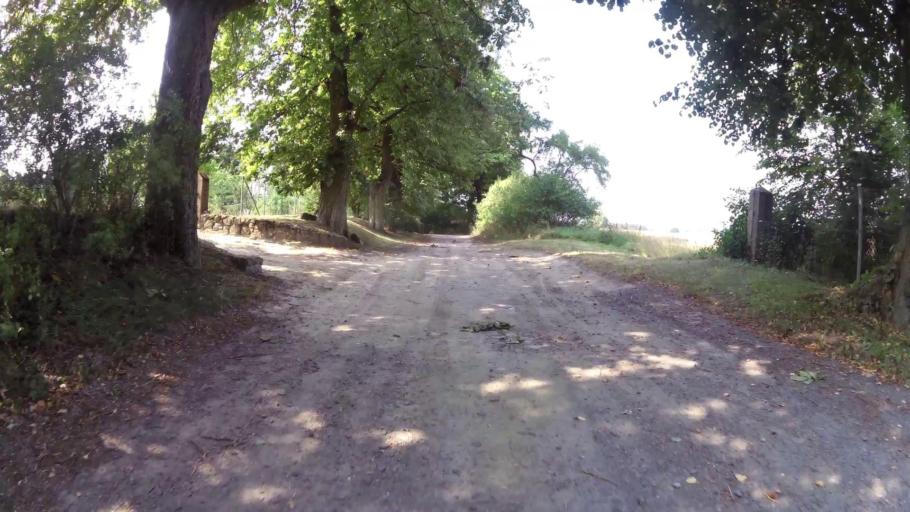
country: PL
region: West Pomeranian Voivodeship
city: Trzcinsko Zdroj
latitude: 52.9232
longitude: 14.5411
